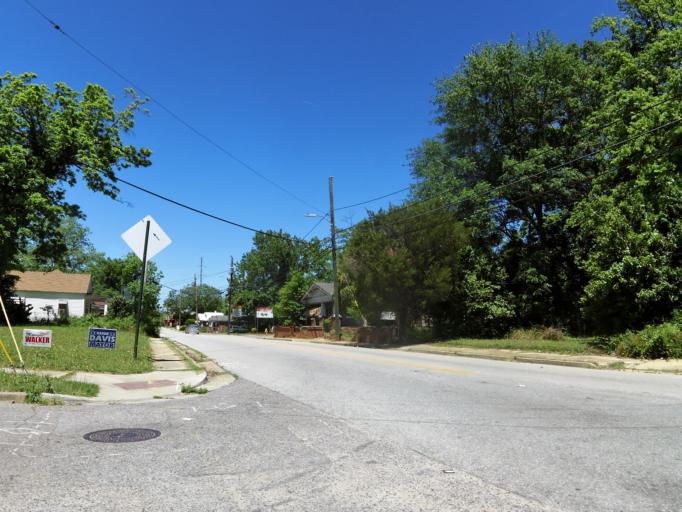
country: US
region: Georgia
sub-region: Richmond County
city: Augusta
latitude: 33.4606
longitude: -81.9788
